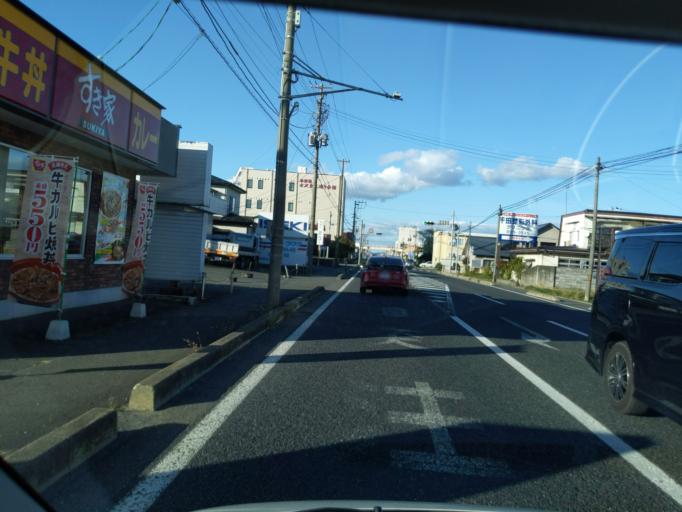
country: JP
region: Iwate
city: Mizusawa
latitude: 39.1365
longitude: 141.1500
